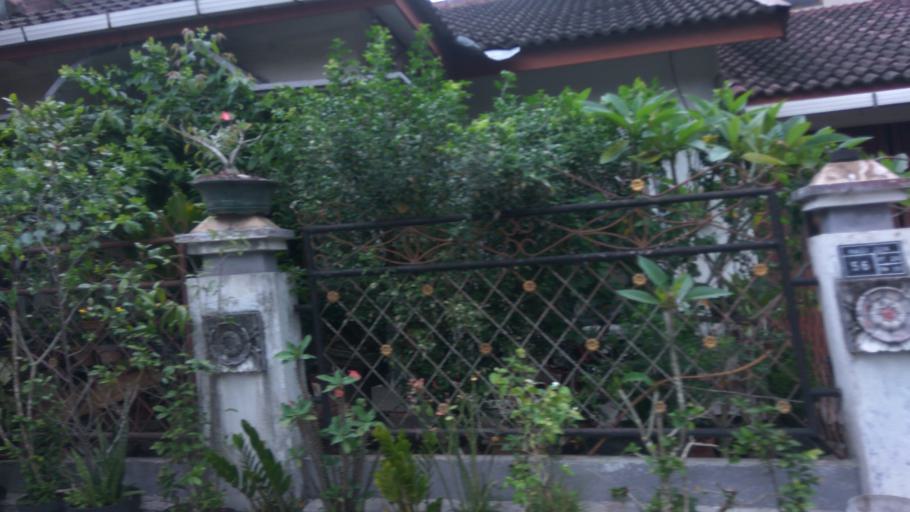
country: ID
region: Daerah Istimewa Yogyakarta
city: Depok
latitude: -7.7391
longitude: 110.4087
